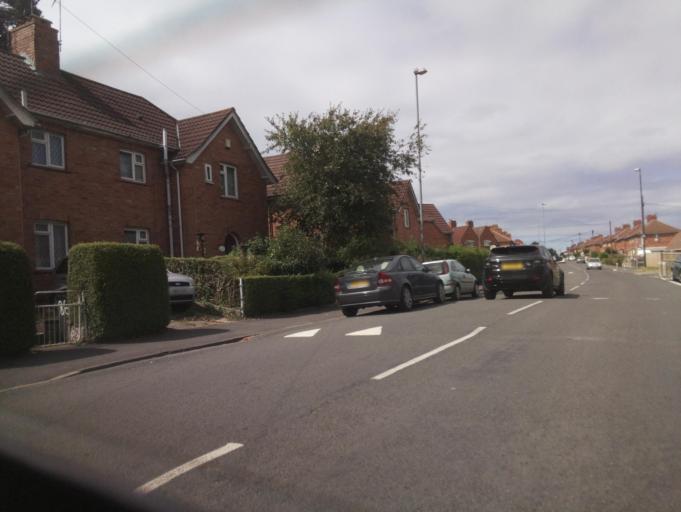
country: GB
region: England
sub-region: Bath and North East Somerset
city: Whitchurch
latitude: 51.4279
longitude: -2.5749
